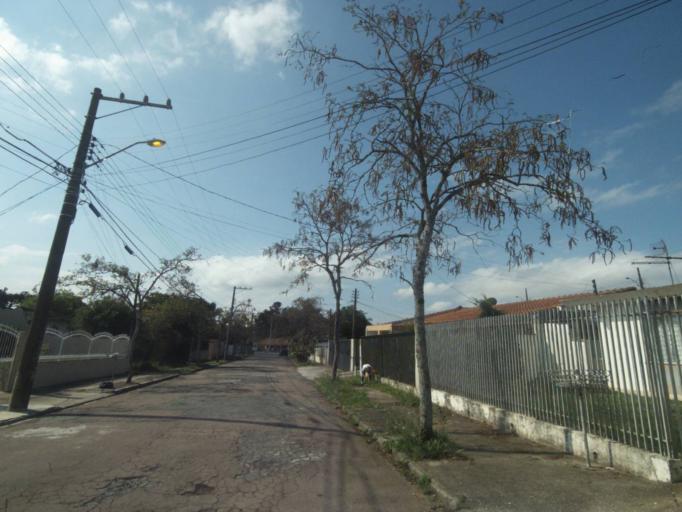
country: BR
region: Parana
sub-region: Pinhais
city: Pinhais
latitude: -25.4035
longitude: -49.2122
